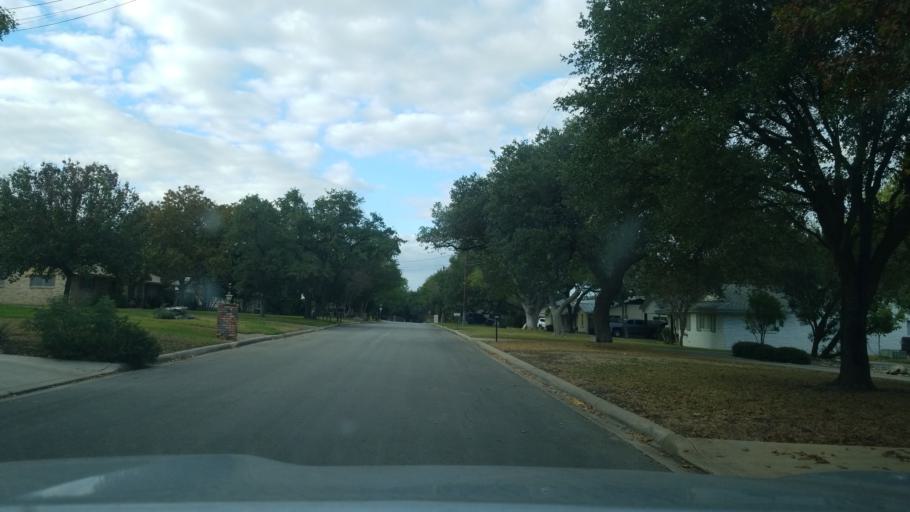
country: US
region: Texas
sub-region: Bexar County
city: Hollywood Park
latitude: 29.6023
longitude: -98.4841
